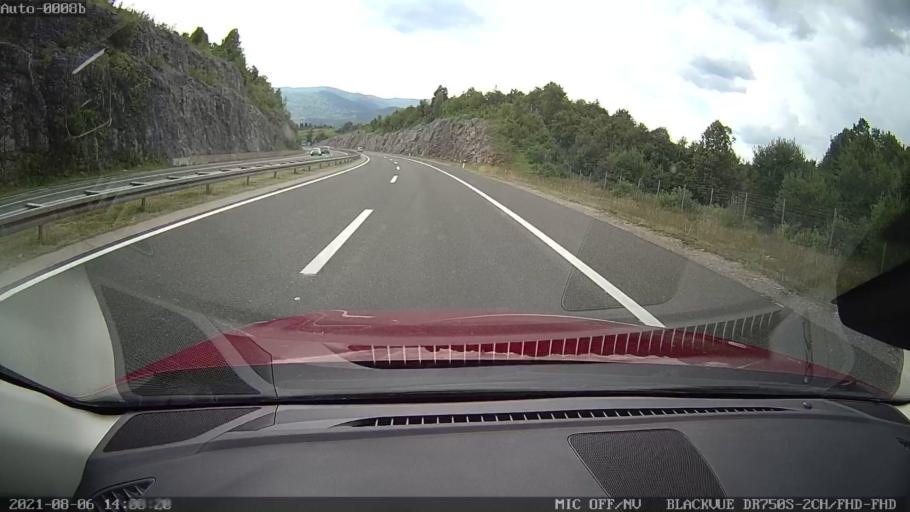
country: HR
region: Primorsko-Goranska
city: Vrbovsko
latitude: 45.3735
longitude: 15.0991
